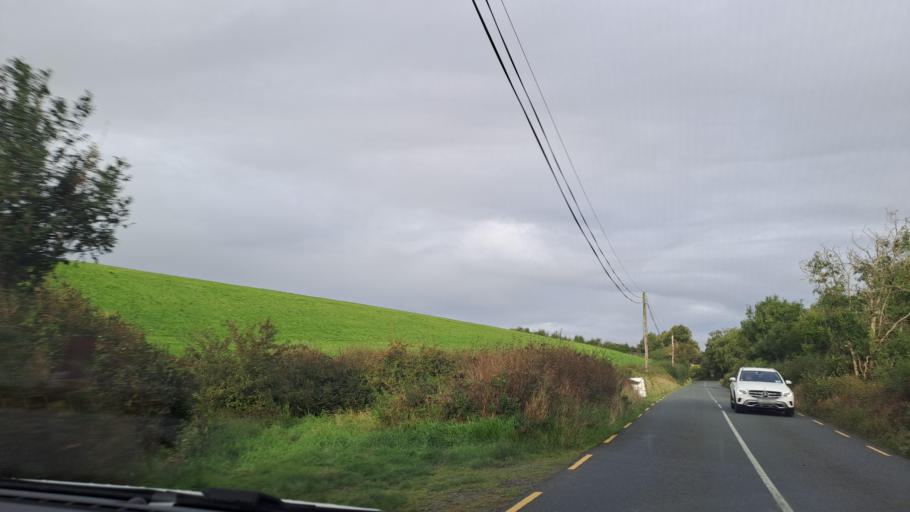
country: IE
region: Ulster
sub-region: An Cabhan
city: Bailieborough
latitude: 53.9975
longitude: -6.8862
